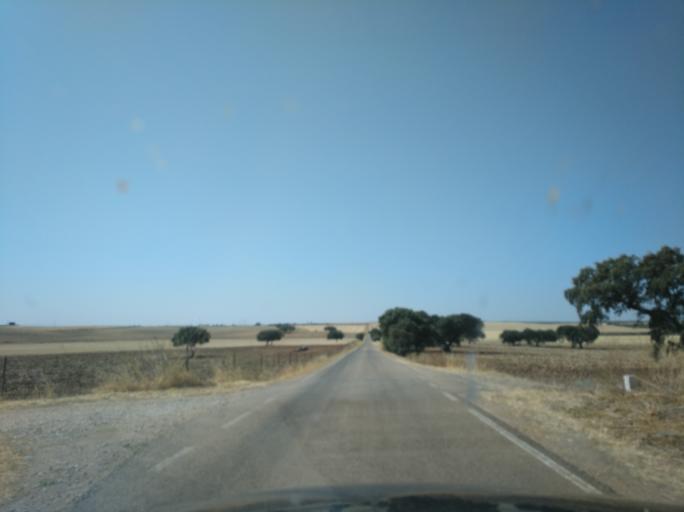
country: PT
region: Portalegre
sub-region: Campo Maior
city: Campo Maior
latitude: 38.9954
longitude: -6.9950
